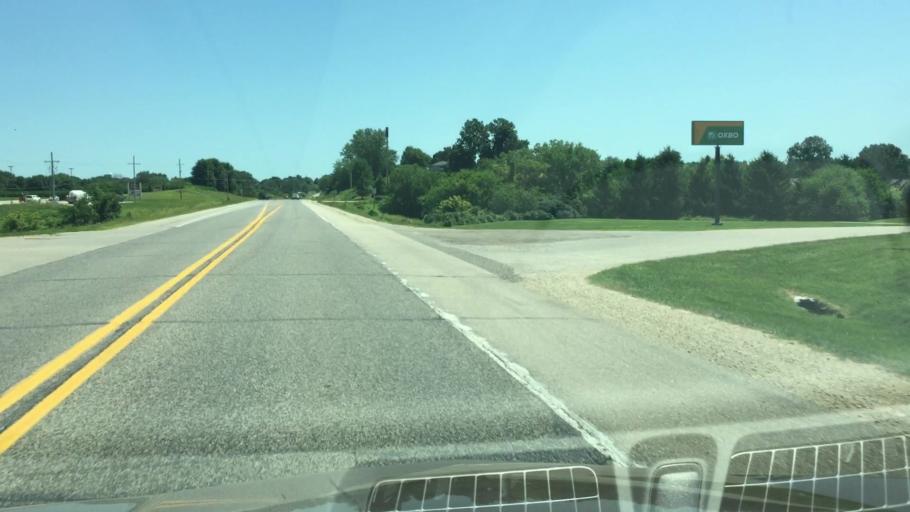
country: US
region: Iowa
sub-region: Linn County
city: Mount Vernon
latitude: 41.9171
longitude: -91.4040
